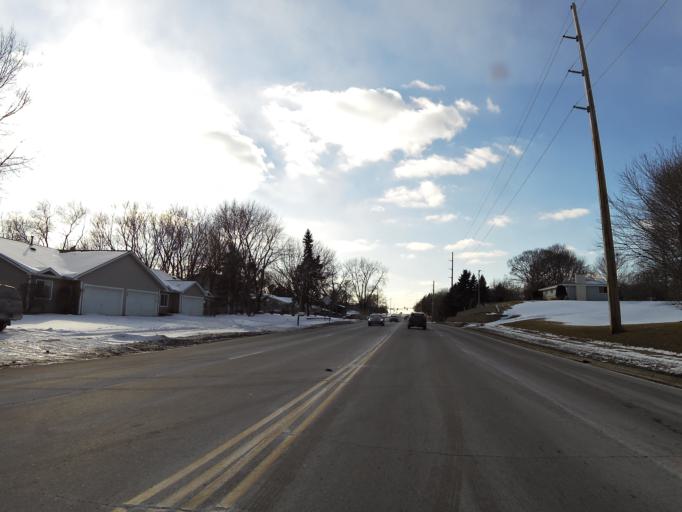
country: US
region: Minnesota
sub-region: Dakota County
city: Burnsville
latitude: 44.7538
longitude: -93.2642
